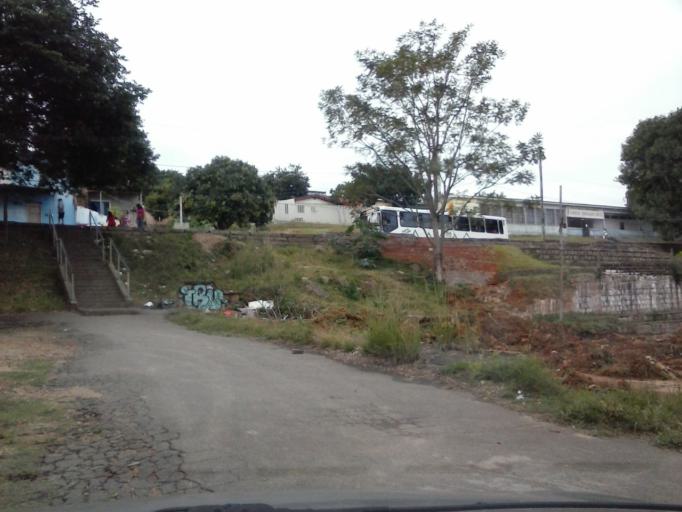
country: BR
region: Rio Grande do Sul
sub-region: Porto Alegre
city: Porto Alegre
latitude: -30.0520
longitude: -51.1507
